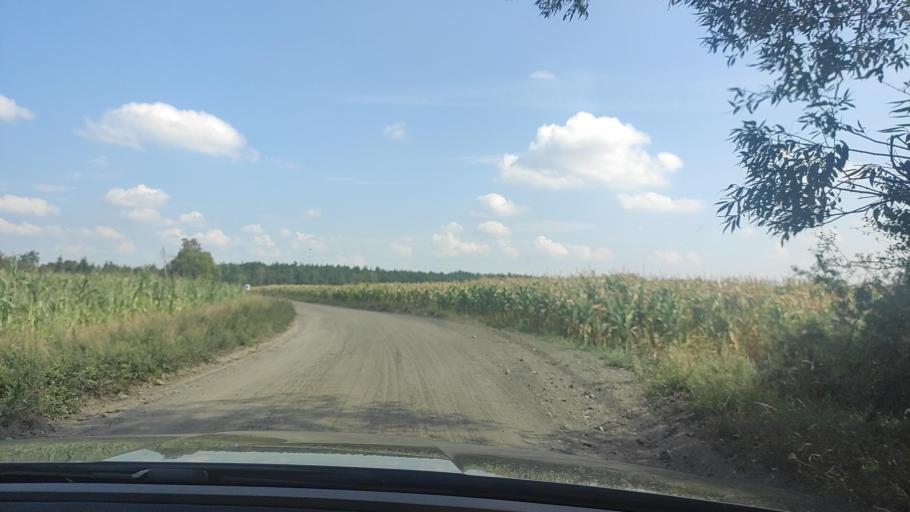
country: PL
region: Greater Poland Voivodeship
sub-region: Powiat poznanski
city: Pobiedziska
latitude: 52.4895
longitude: 17.1979
